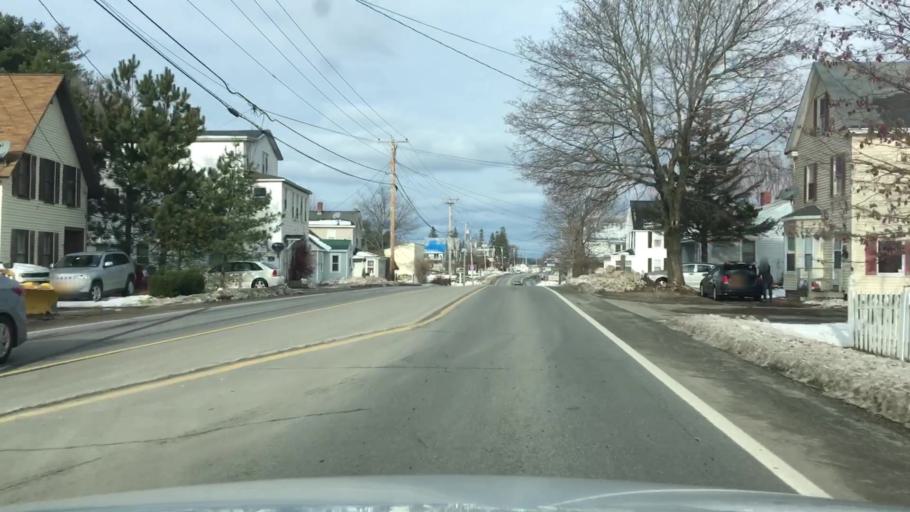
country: US
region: Maine
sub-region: Kennebec County
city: Winthrop
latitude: 44.3015
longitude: -69.9791
